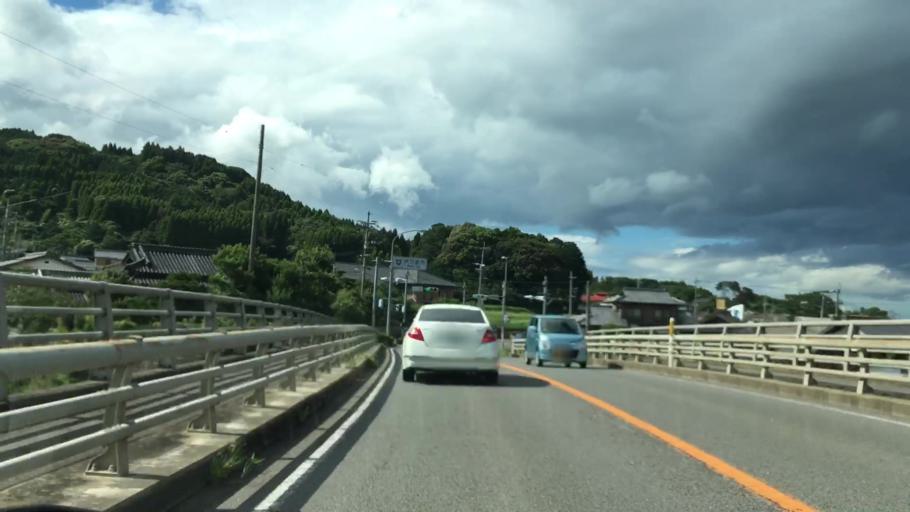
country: JP
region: Saga Prefecture
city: Imaricho-ko
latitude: 33.2411
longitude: 129.8508
